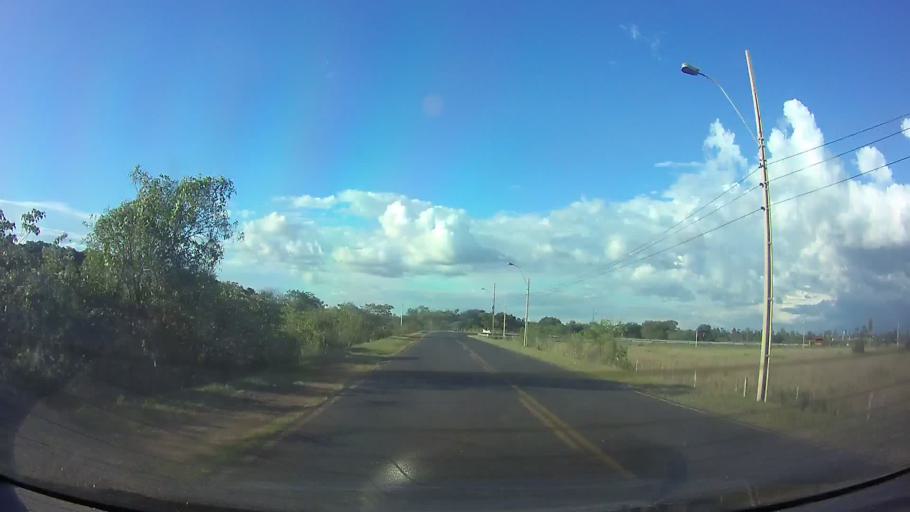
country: PY
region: Cordillera
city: Emboscada
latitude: -25.1460
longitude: -57.2602
